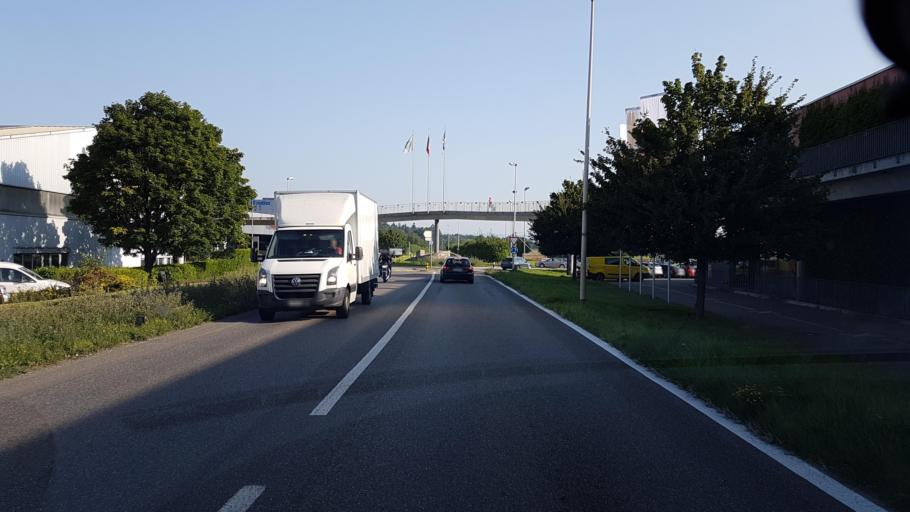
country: CH
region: Aargau
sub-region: Bezirk Baden
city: Wurenlingen
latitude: 47.5251
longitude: 8.2437
